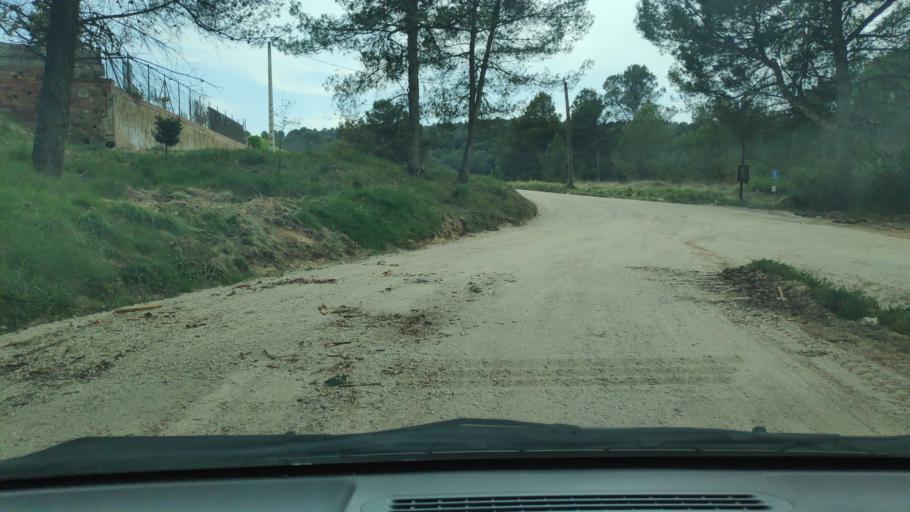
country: ES
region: Catalonia
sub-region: Provincia de Barcelona
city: Rubi
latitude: 41.5106
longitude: 2.0566
